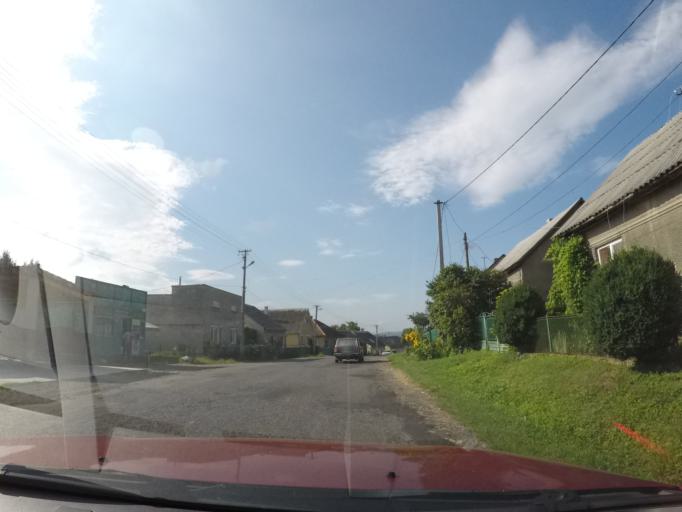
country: UA
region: Zakarpattia
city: Velykyi Bereznyi
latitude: 48.9127
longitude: 22.4605
